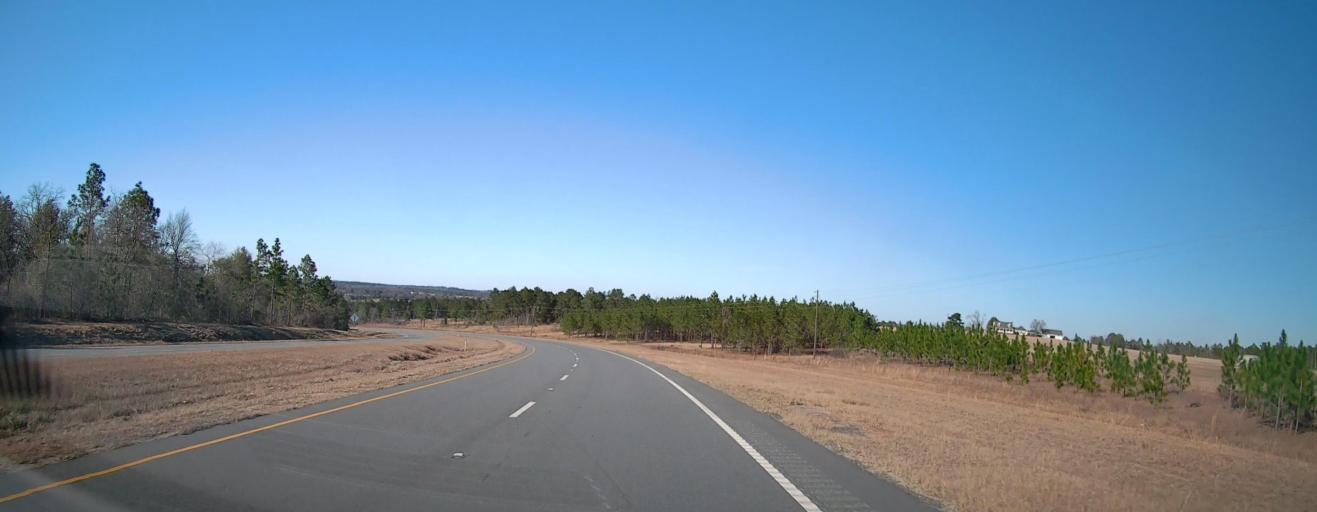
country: US
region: Georgia
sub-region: Taylor County
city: Butler
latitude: 32.6096
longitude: -84.2374
